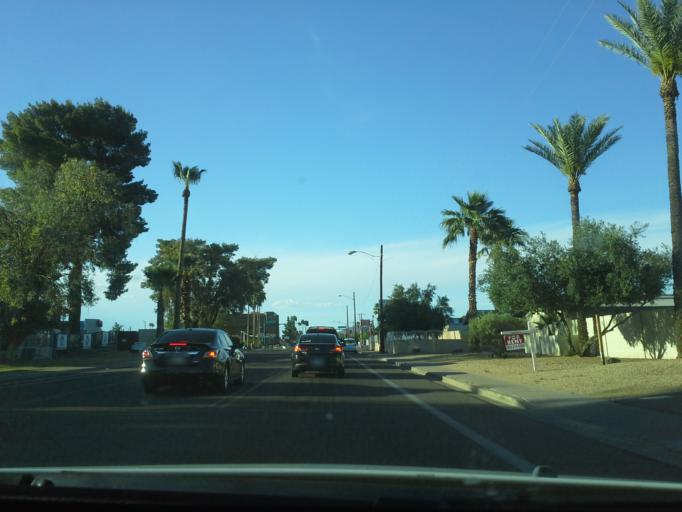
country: US
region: Arizona
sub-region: Maricopa County
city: Phoenix
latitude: 33.5076
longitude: -112.0912
